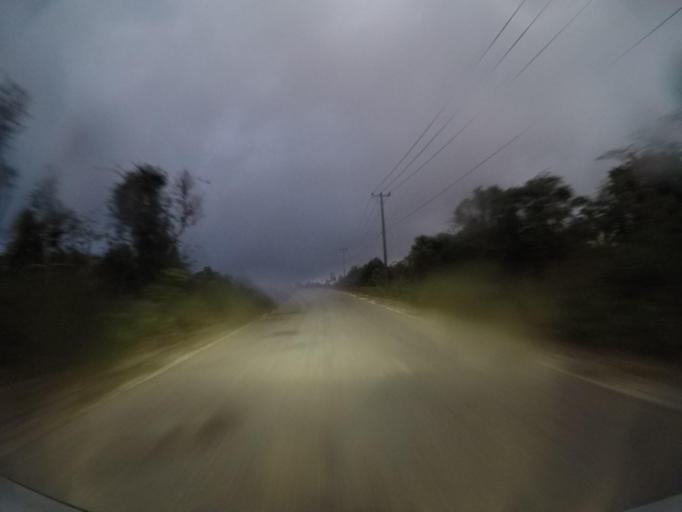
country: TL
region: Lautem
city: Lospalos
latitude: -8.4118
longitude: 126.9983
